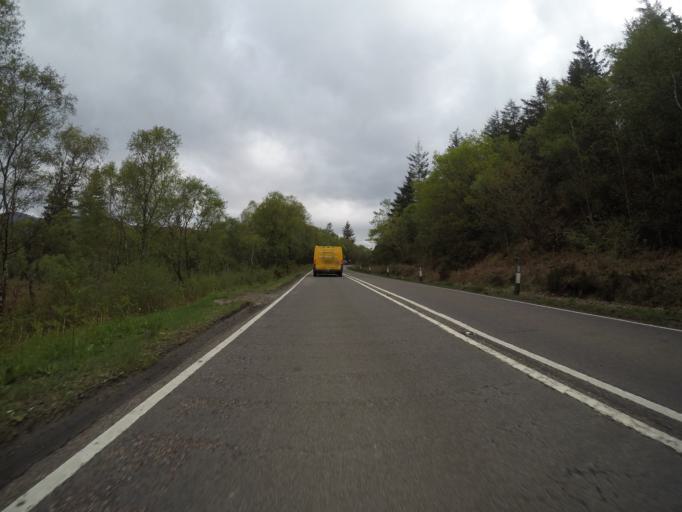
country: GB
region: Scotland
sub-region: Highland
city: Fort William
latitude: 56.7450
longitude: -5.2030
